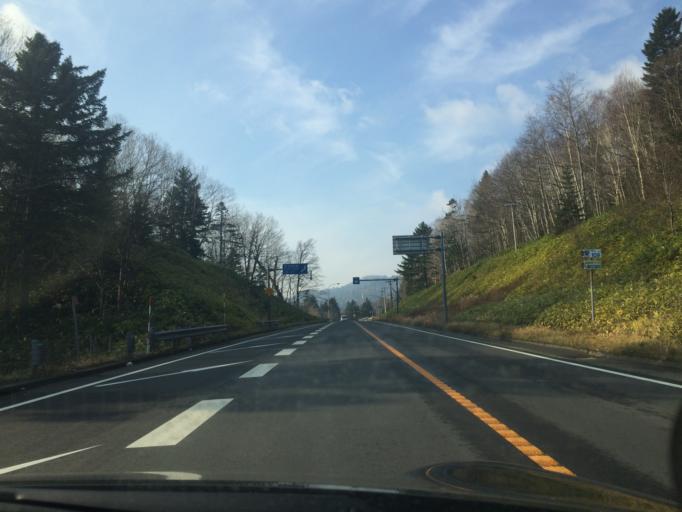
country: JP
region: Hokkaido
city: Shimo-furano
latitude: 42.9108
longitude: 142.3606
